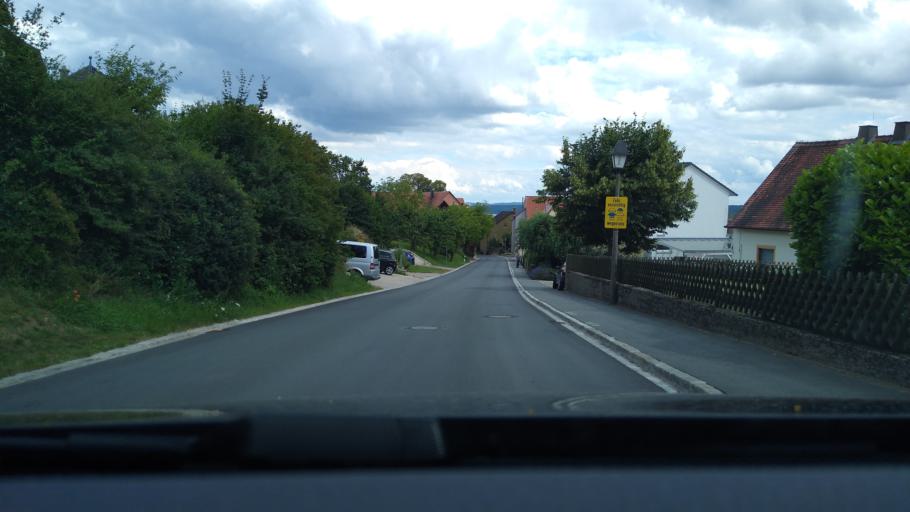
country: DE
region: Bavaria
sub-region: Regierungsbezirk Mittelfranken
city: Absberg
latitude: 49.1456
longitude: 10.8691
